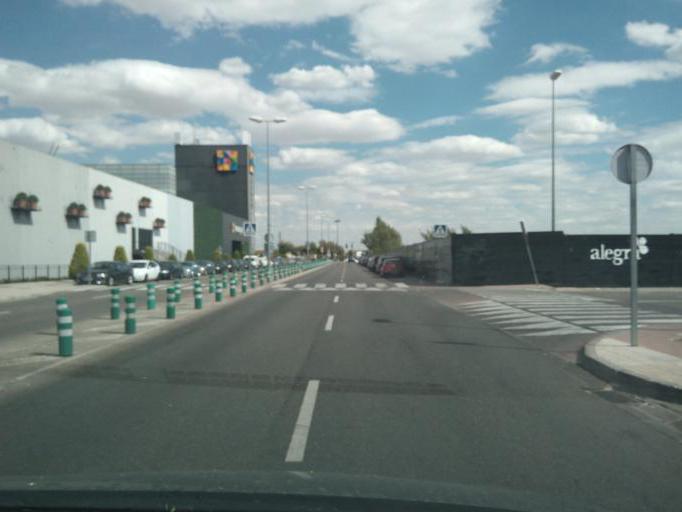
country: ES
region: Madrid
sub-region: Provincia de Madrid
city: San Sebastian de los Reyes
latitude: 40.5667
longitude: -3.6085
